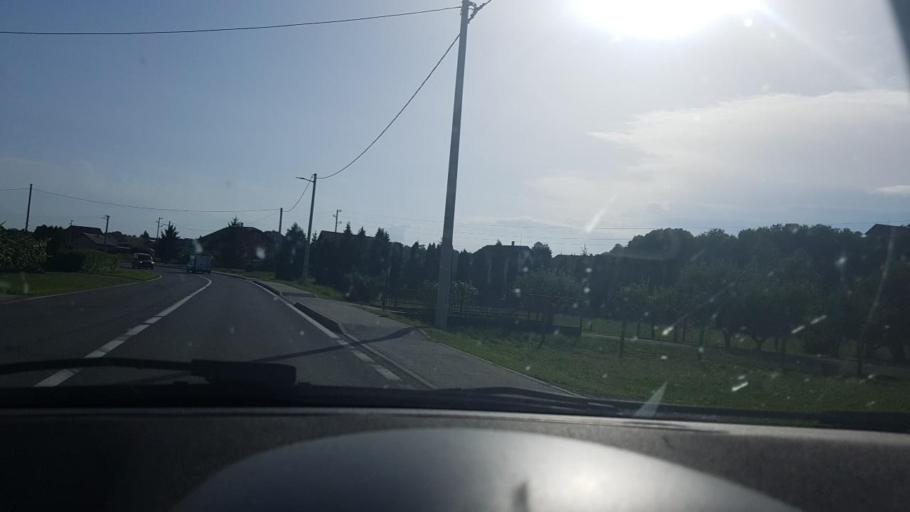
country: HR
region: Krapinsko-Zagorska
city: Bedekovcina
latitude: 46.0295
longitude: 15.9643
